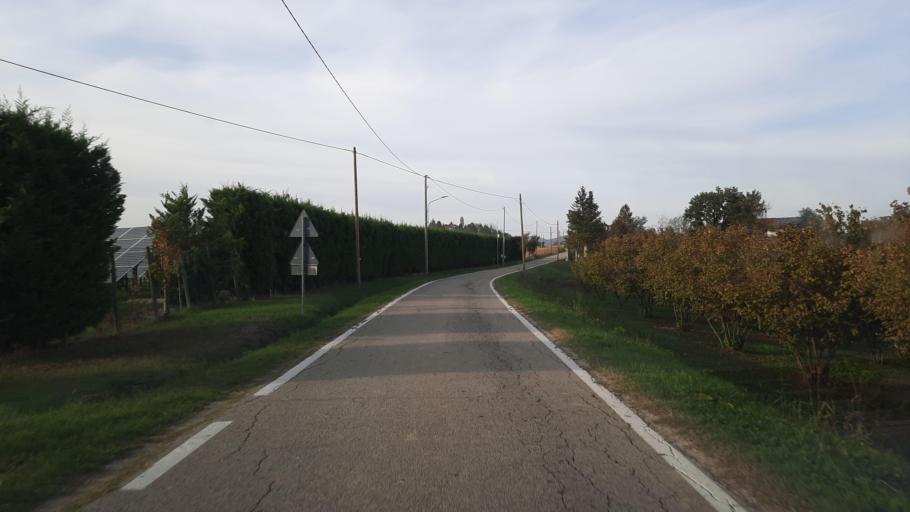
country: IT
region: Piedmont
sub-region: Provincia di Asti
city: Tonco
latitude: 45.0148
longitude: 8.2062
